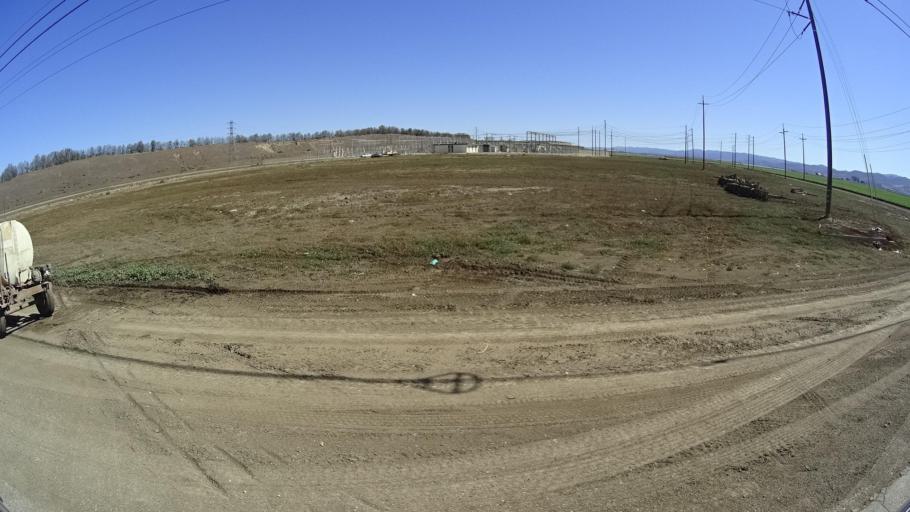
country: US
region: California
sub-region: Monterey County
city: King City
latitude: 36.2667
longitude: -121.1481
